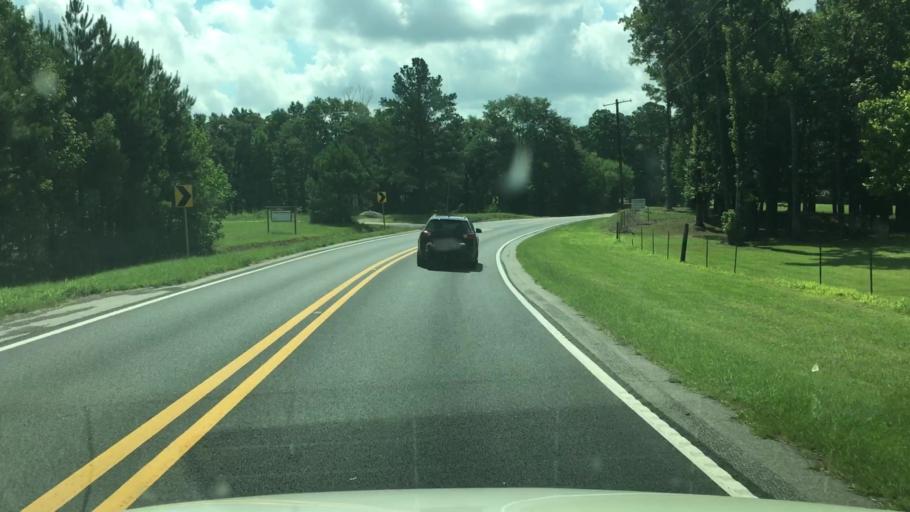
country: US
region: Arkansas
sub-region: Clark County
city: Arkadelphia
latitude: 34.2543
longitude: -93.1250
